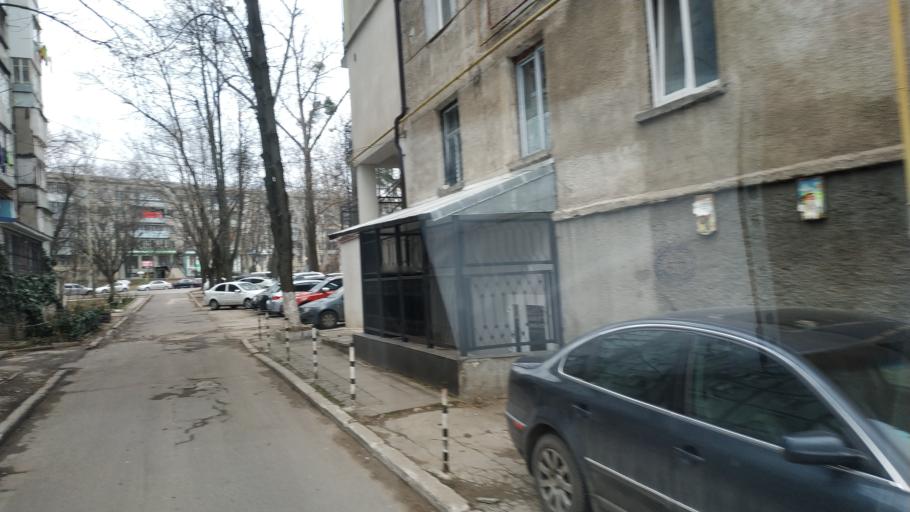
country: MD
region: Chisinau
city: Chisinau
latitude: 47.0288
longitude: 28.7911
